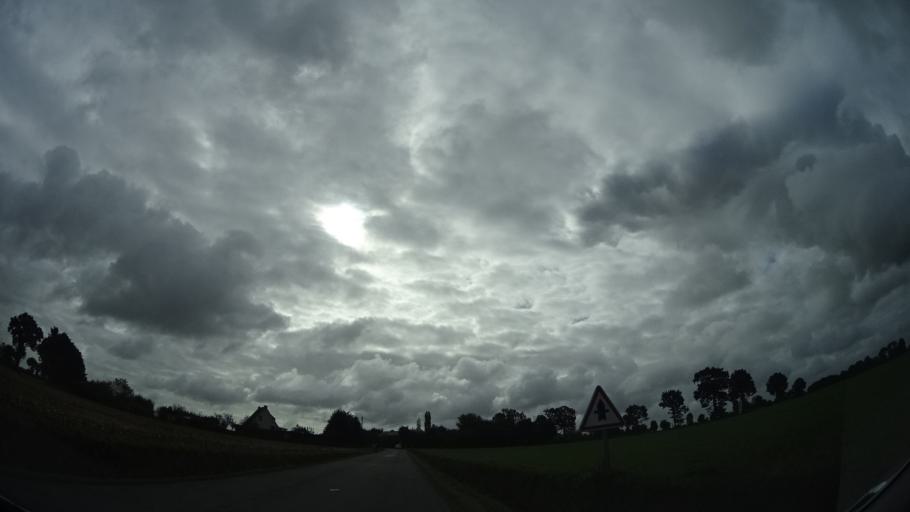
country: FR
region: Brittany
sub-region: Departement d'Ille-et-Vilaine
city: Montreuil-sur-Ille
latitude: 48.2988
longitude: -1.6484
